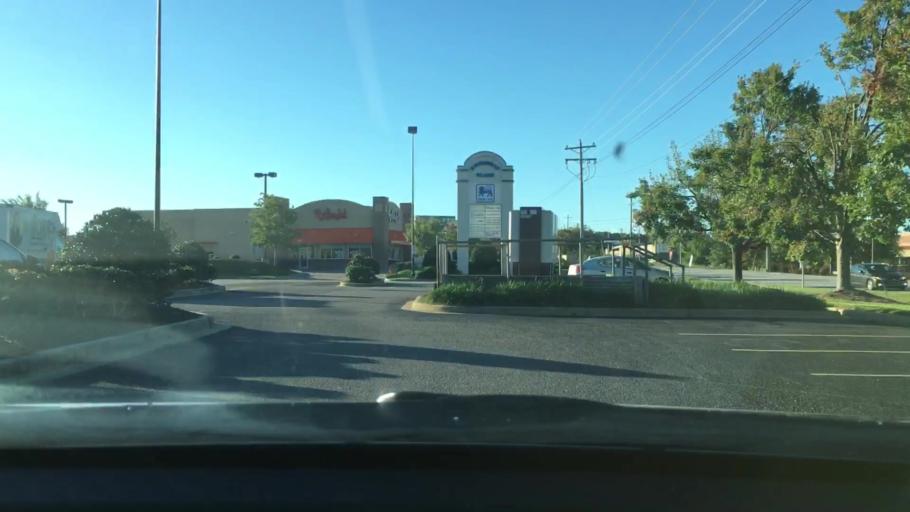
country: US
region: South Carolina
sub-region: Lexington County
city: Irmo
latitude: 34.0952
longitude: -81.1587
